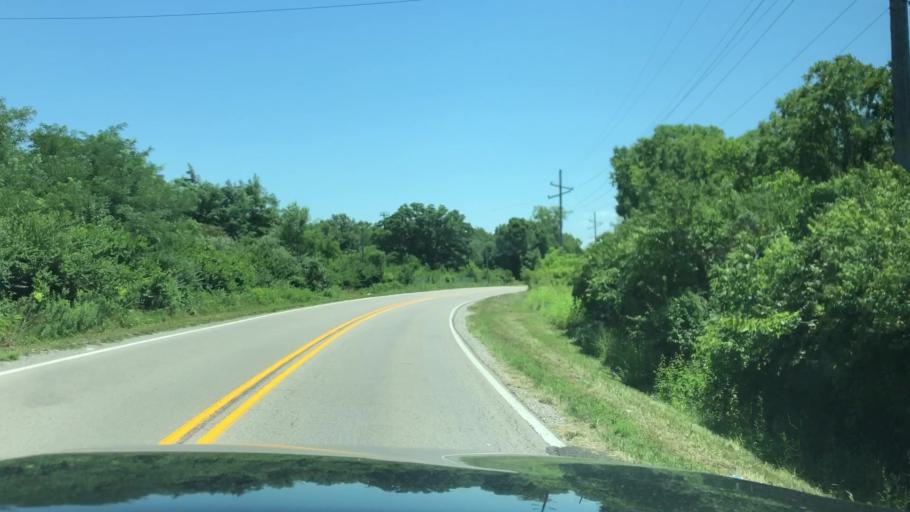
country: US
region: Illinois
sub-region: Saint Clair County
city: Alorton
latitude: 38.5522
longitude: -90.0757
